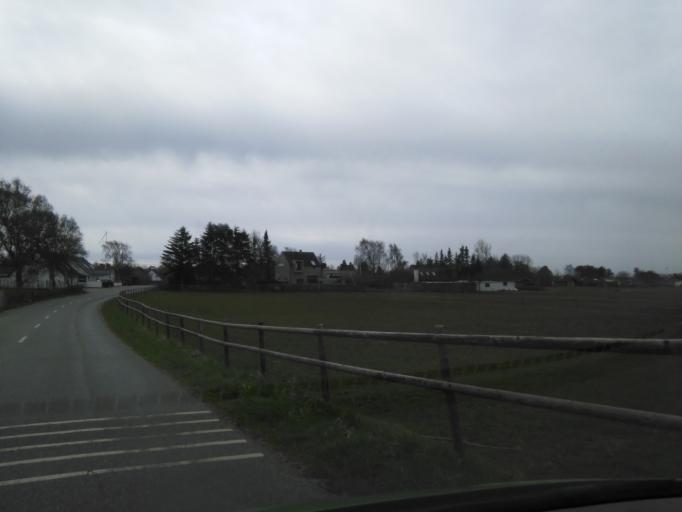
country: DK
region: Central Jutland
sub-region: Arhus Kommune
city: Beder
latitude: 56.0267
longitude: 10.2607
